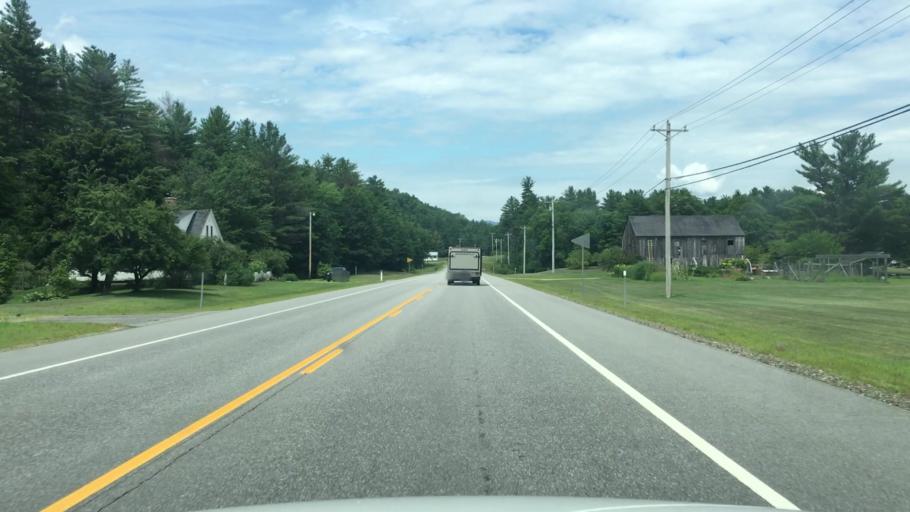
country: US
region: New Hampshire
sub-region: Grafton County
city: Rumney
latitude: 43.8317
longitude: -71.8974
